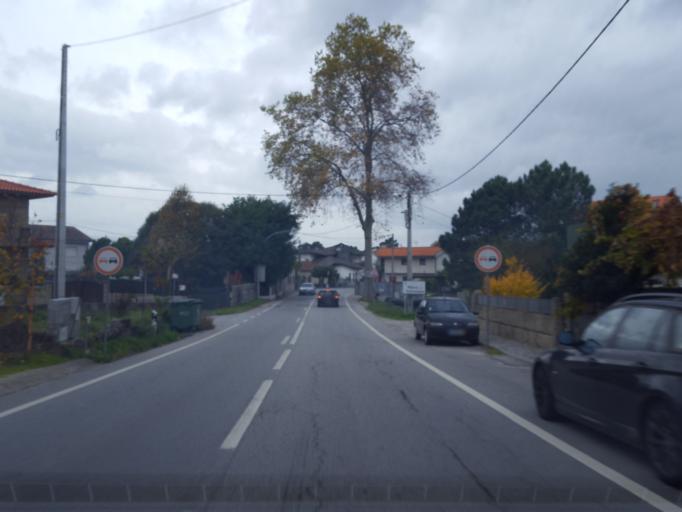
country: PT
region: Porto
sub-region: Marco de Canaveses
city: Marco de Canavezes
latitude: 41.1689
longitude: -8.1499
